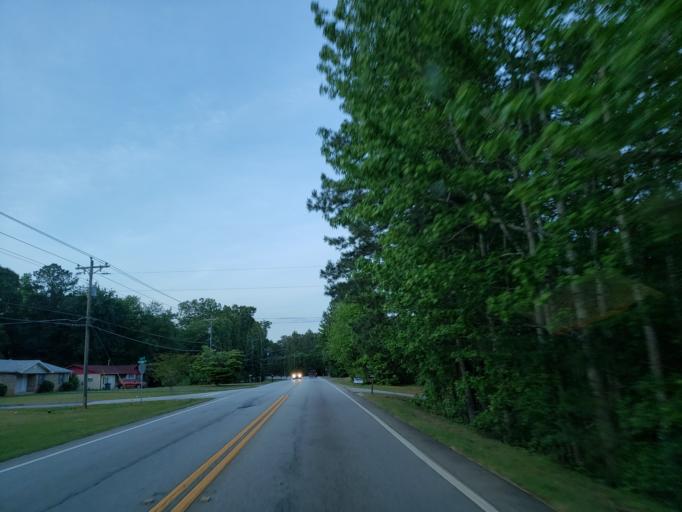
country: US
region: Georgia
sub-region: Douglas County
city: Douglasville
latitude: 33.6648
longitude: -84.8079
